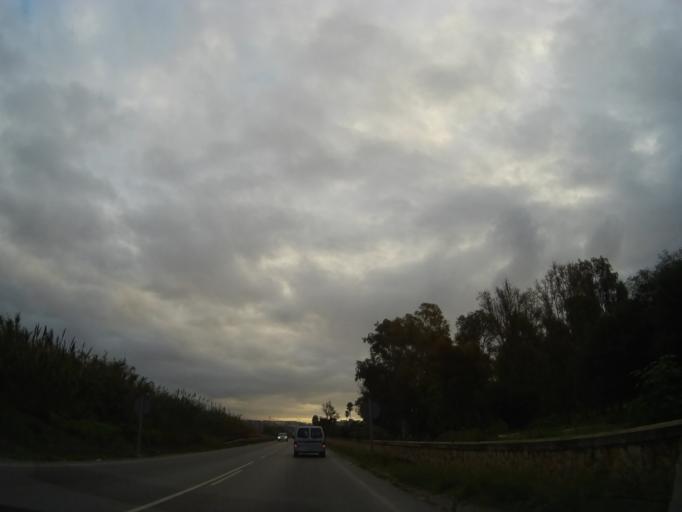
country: ES
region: Andalusia
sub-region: Provincia de Malaga
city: Alhaurin de la Torre
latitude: 36.7072
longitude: -4.4998
